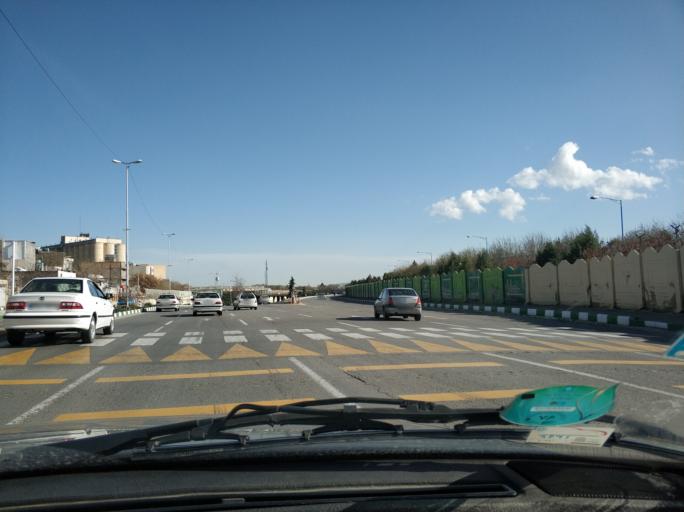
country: IR
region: Razavi Khorasan
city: Mashhad
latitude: 36.3077
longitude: 59.6261
